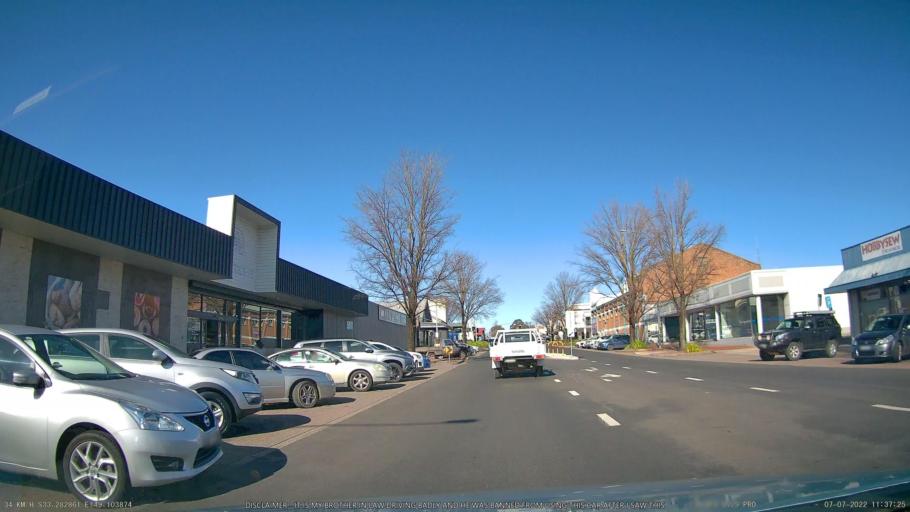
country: AU
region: New South Wales
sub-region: Orange Municipality
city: Orange
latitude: -33.2831
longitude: 149.1038
